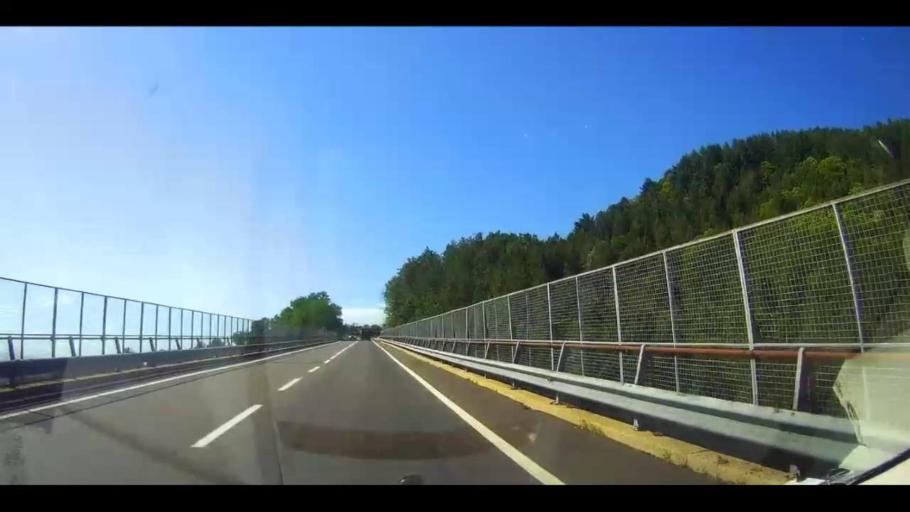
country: IT
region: Calabria
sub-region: Provincia di Cosenza
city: Celico
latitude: 39.3224
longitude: 16.3662
